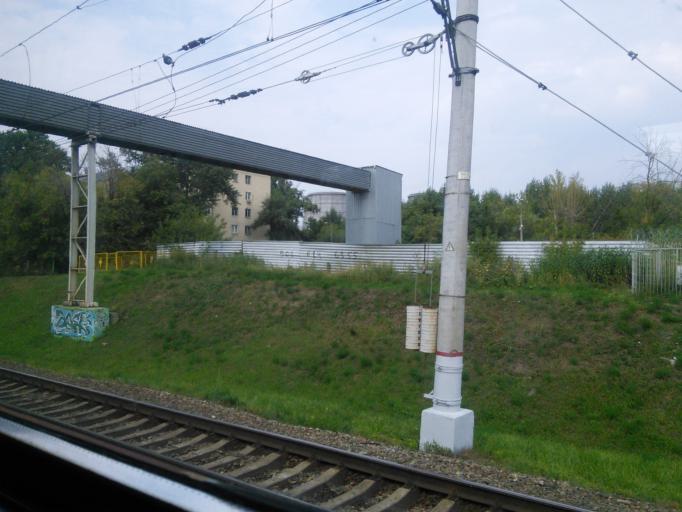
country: RU
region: Moscow
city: Lefortovo
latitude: 55.7488
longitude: 37.7266
